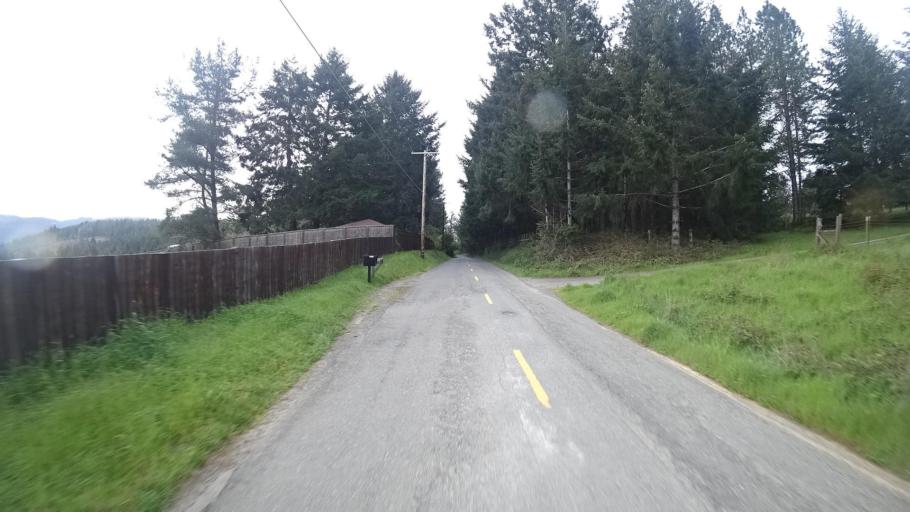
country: US
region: California
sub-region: Humboldt County
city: Redway
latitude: 40.2968
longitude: -123.8208
